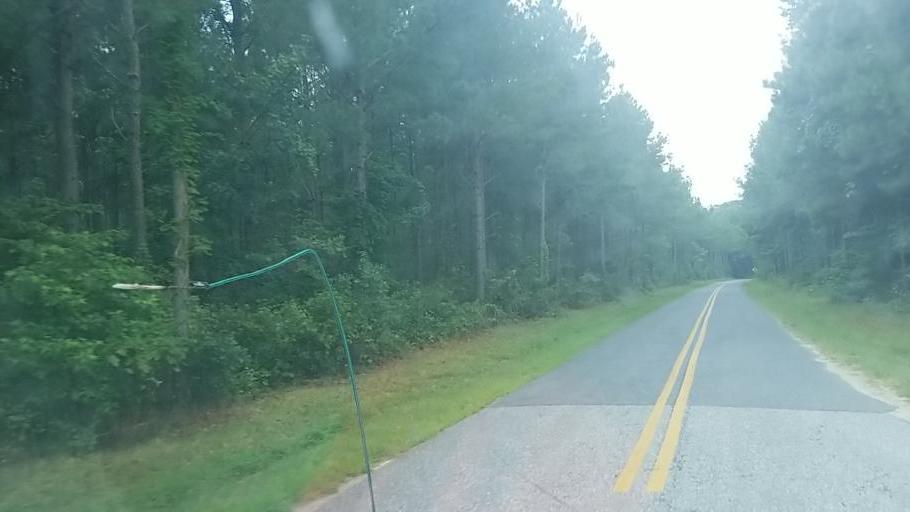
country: US
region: Maryland
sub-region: Worcester County
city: Snow Hill
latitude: 38.2615
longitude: -75.4541
